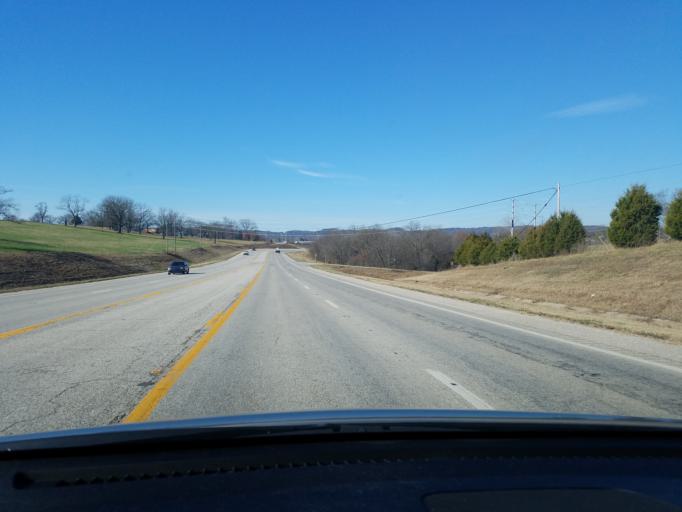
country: US
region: Arkansas
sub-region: Carroll County
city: Berryville
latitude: 36.3903
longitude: -93.6270
